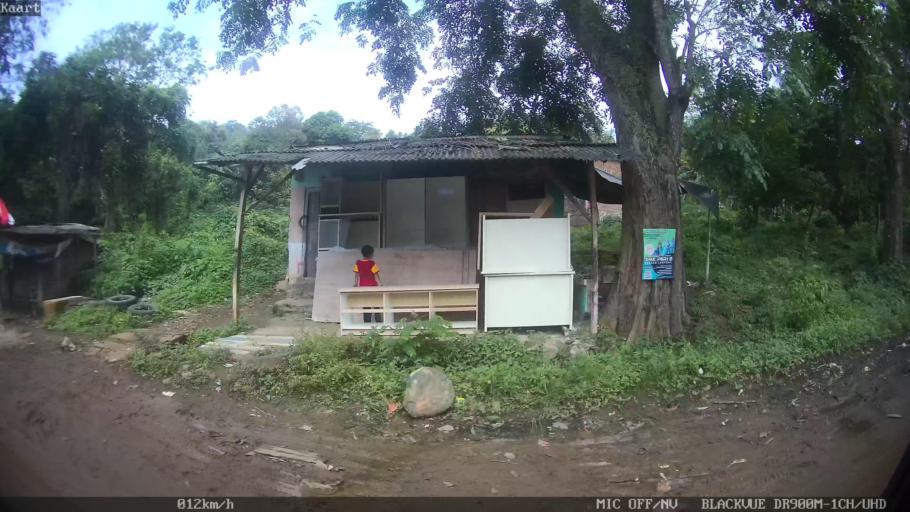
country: ID
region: Lampung
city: Bandarlampung
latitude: -5.4560
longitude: 105.2457
